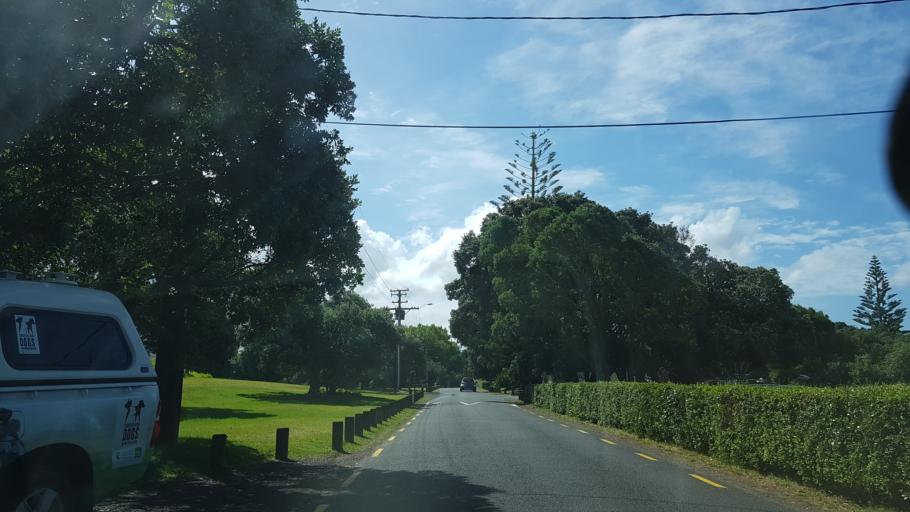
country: NZ
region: Auckland
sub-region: Auckland
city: Rothesay Bay
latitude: -36.6850
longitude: 174.7492
